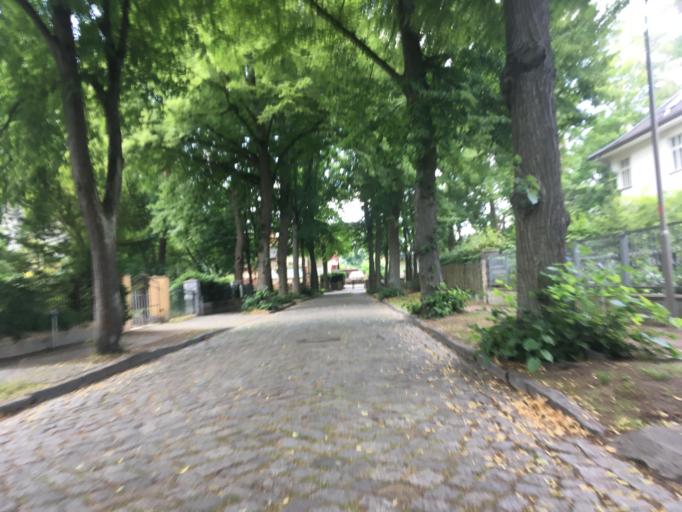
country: DE
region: Brandenburg
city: Zeuthen
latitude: 52.3429
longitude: 13.6280
